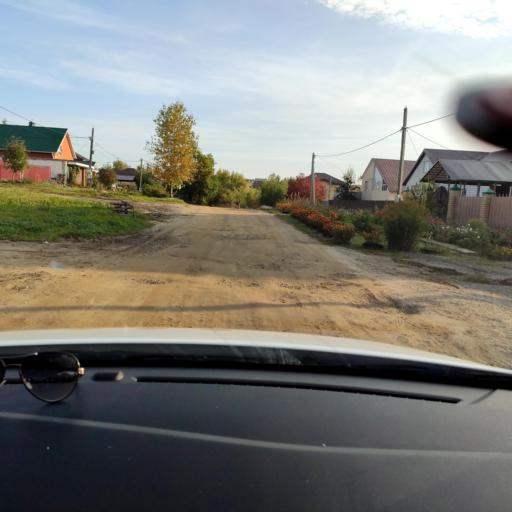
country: RU
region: Tatarstan
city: Vysokaya Gora
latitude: 55.8175
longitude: 49.2627
